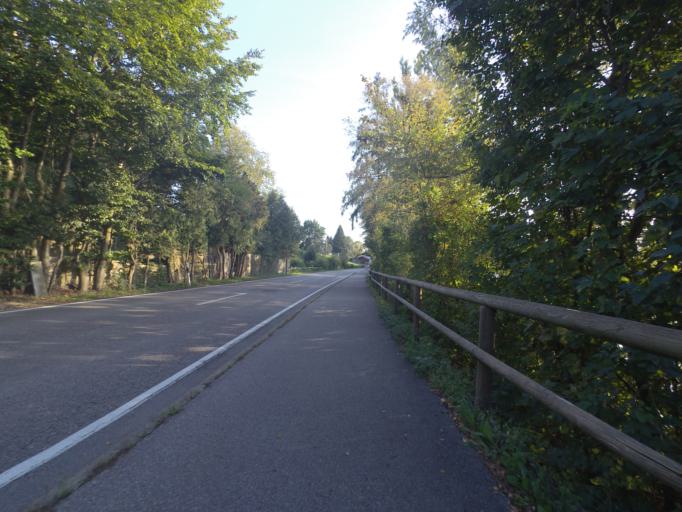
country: DE
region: Bavaria
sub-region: Upper Bavaria
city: Laufen
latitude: 47.9102
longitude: 12.9147
